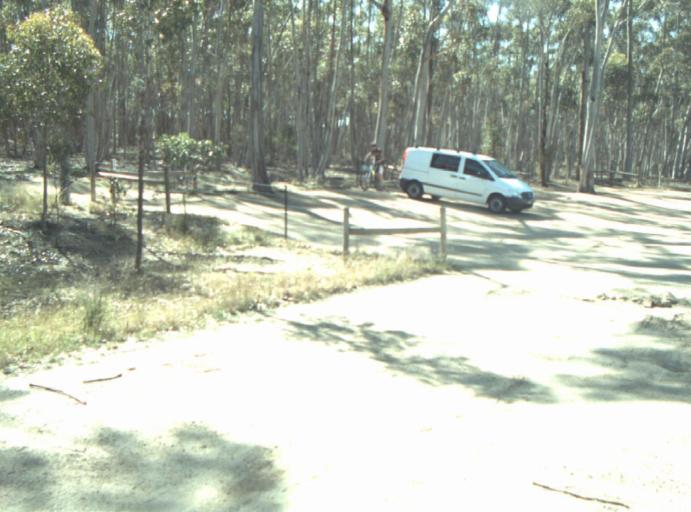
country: AU
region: Victoria
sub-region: Greater Geelong
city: Lara
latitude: -37.9634
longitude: 144.4049
